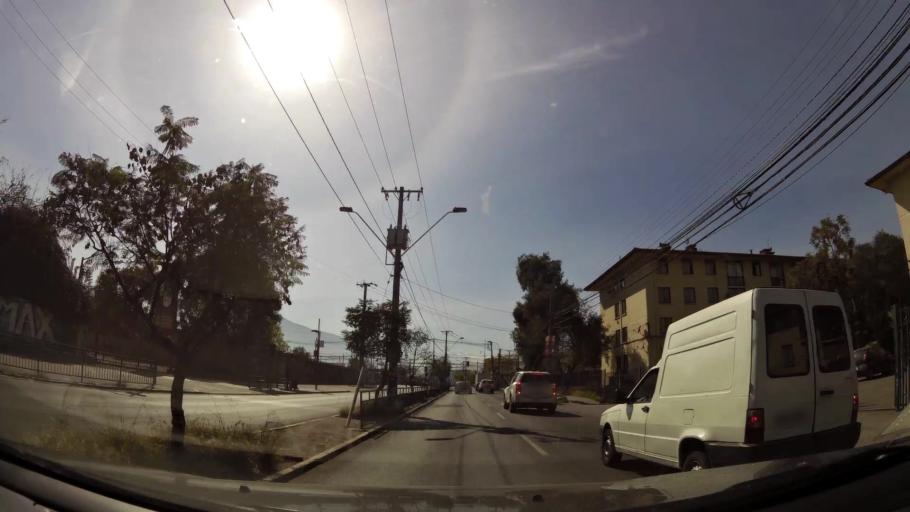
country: CL
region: Santiago Metropolitan
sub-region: Provincia de Cordillera
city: Puente Alto
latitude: -33.6031
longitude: -70.5783
